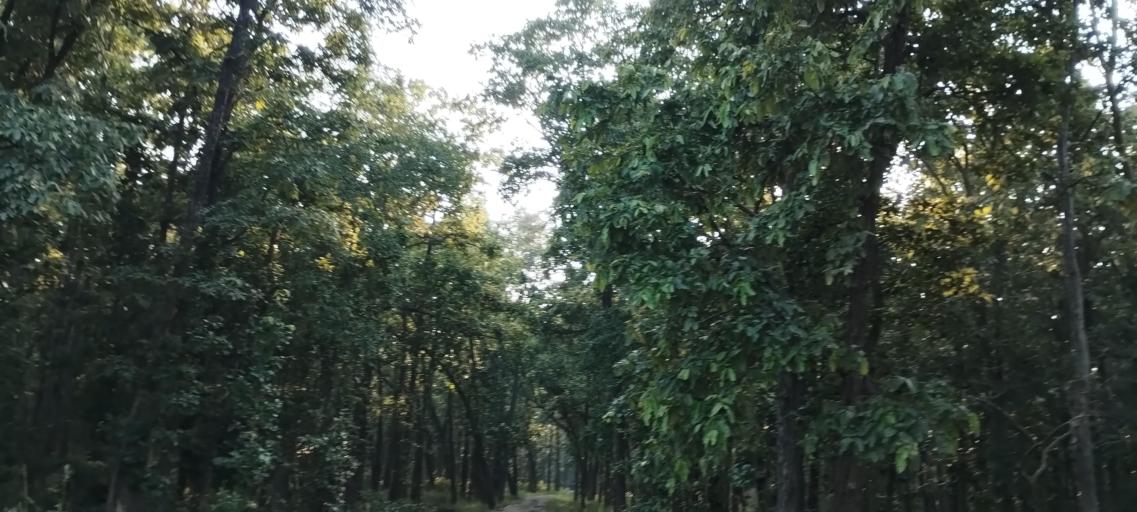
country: NP
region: Far Western
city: Tikapur
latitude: 28.5031
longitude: 81.2744
